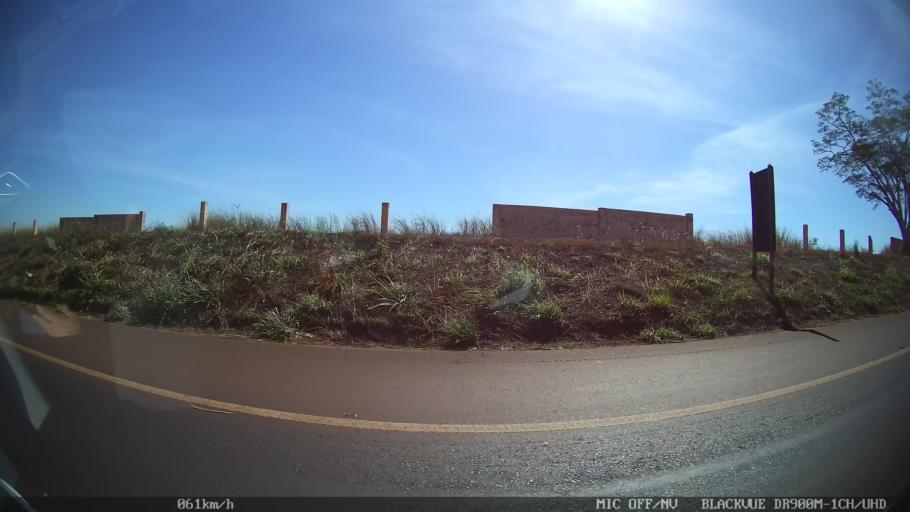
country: BR
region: Sao Paulo
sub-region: Barretos
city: Barretos
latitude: -20.4478
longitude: -48.4514
